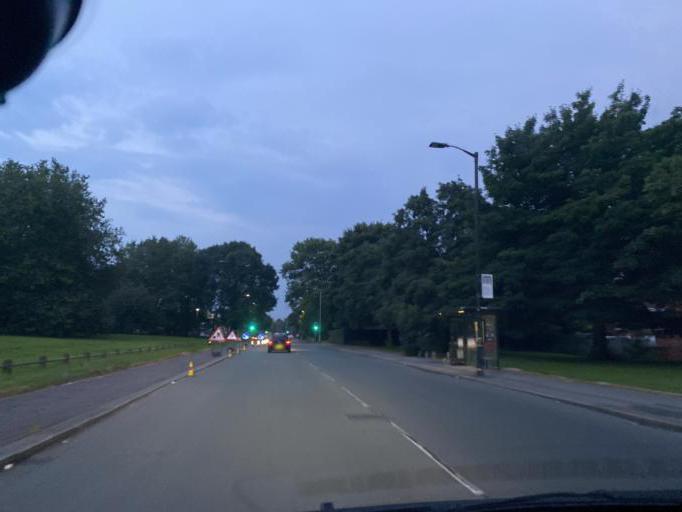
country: GB
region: England
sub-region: Manchester
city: Hulme
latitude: 53.4612
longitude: -2.2581
